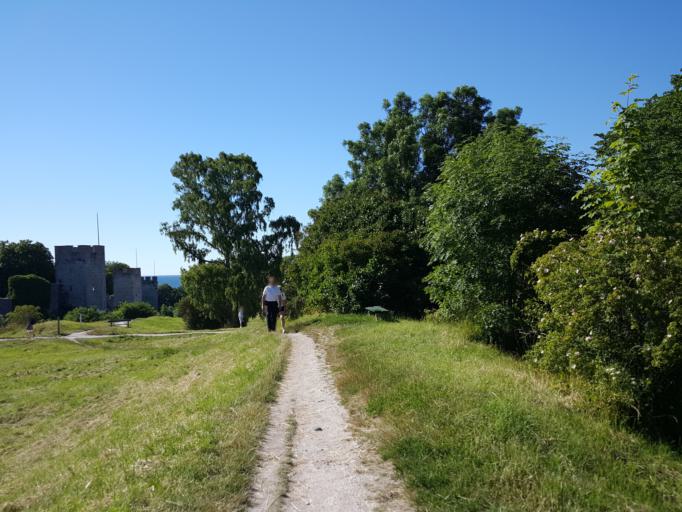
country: SE
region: Gotland
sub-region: Gotland
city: Visby
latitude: 57.6454
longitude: 18.3007
